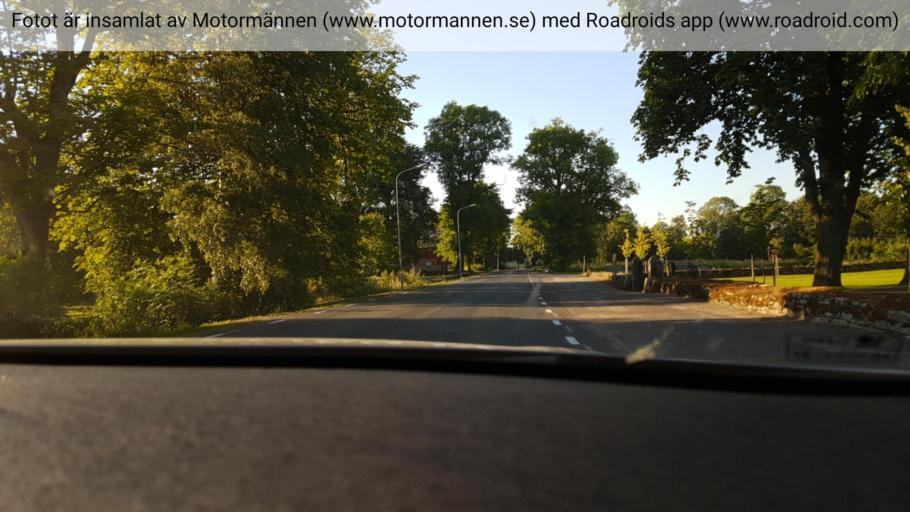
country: SE
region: Vaestra Goetaland
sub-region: Skovde Kommun
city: Skultorp
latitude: 58.2515
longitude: 13.7842
